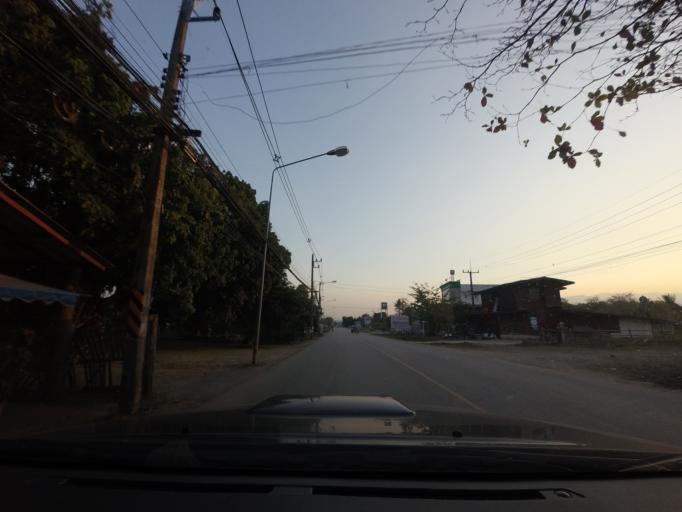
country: TH
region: Chiang Mai
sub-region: Amphoe Chiang Dao
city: Chiang Dao
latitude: 19.3628
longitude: 98.9644
